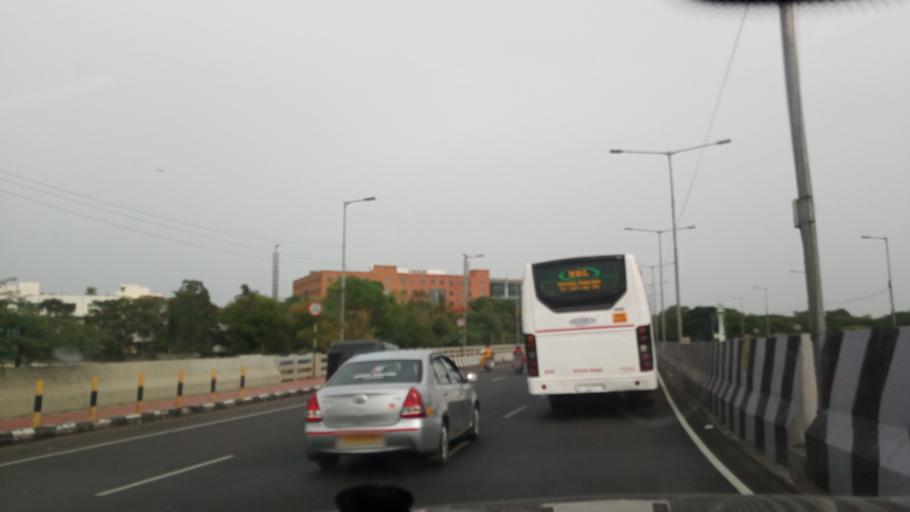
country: IN
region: Tamil Nadu
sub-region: Kancheepuram
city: Manappakkam
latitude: 13.0201
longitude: 80.1858
